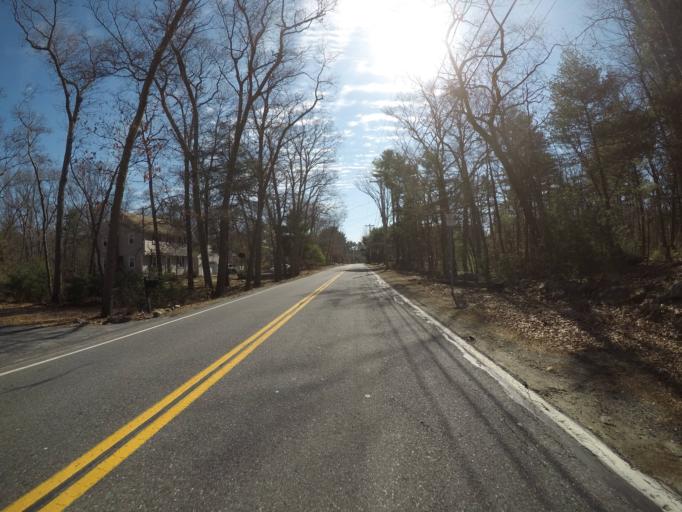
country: US
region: Massachusetts
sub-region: Bristol County
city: Easton
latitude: 42.0649
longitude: -71.1344
